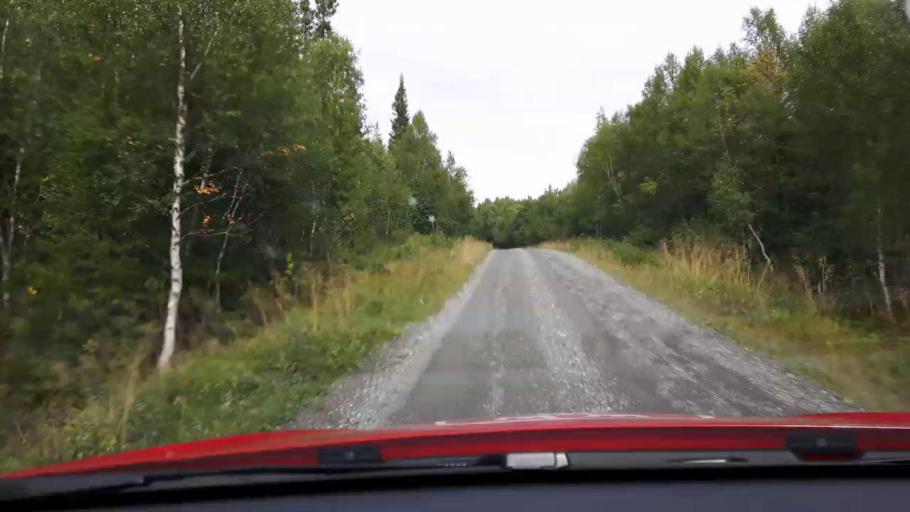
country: SE
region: Jaemtland
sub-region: Are Kommun
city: Are
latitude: 63.7834
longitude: 13.1031
